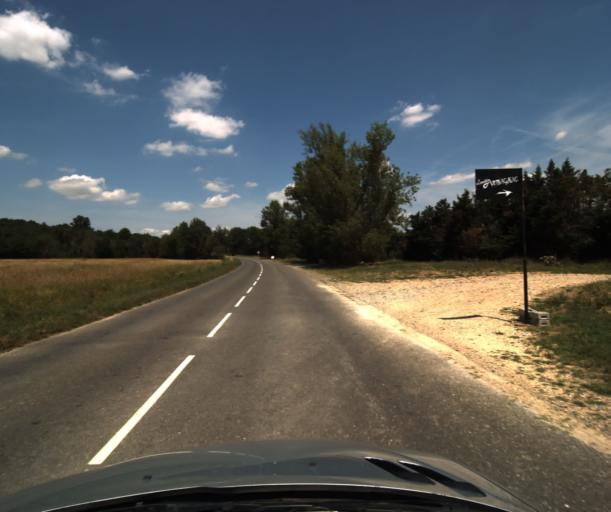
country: FR
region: Midi-Pyrenees
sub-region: Departement de la Haute-Garonne
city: Saint-Lys
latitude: 43.4890
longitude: 1.2124
